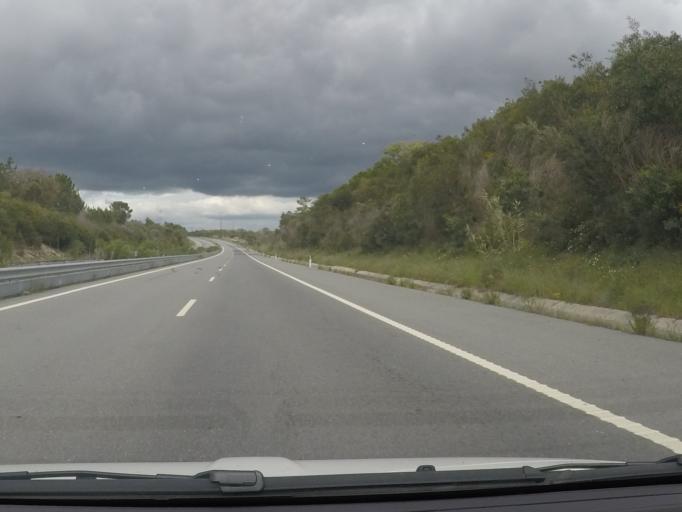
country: PT
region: Setubal
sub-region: Santiago do Cacem
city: Santo Andre
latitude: 37.9872
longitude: -8.7775
